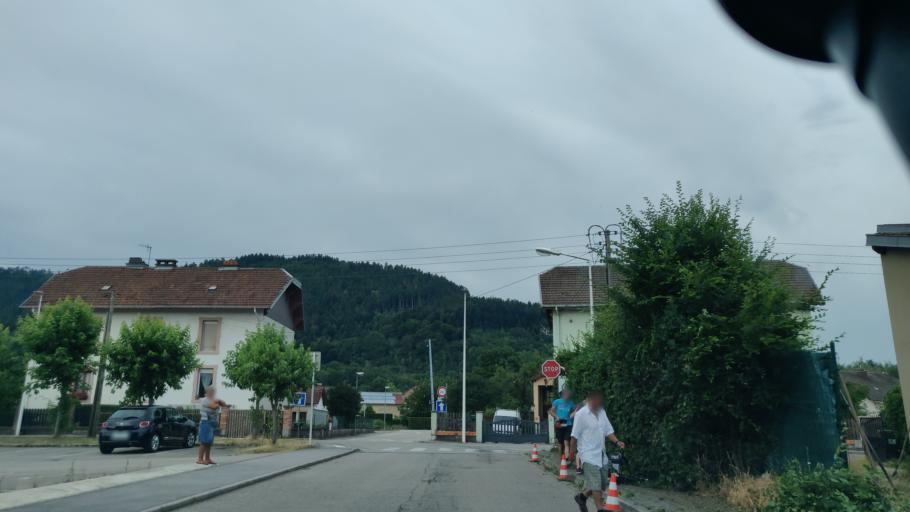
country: FR
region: Lorraine
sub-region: Departement des Vosges
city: Saint-Die-des-Vosges
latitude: 48.2885
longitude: 6.9391
